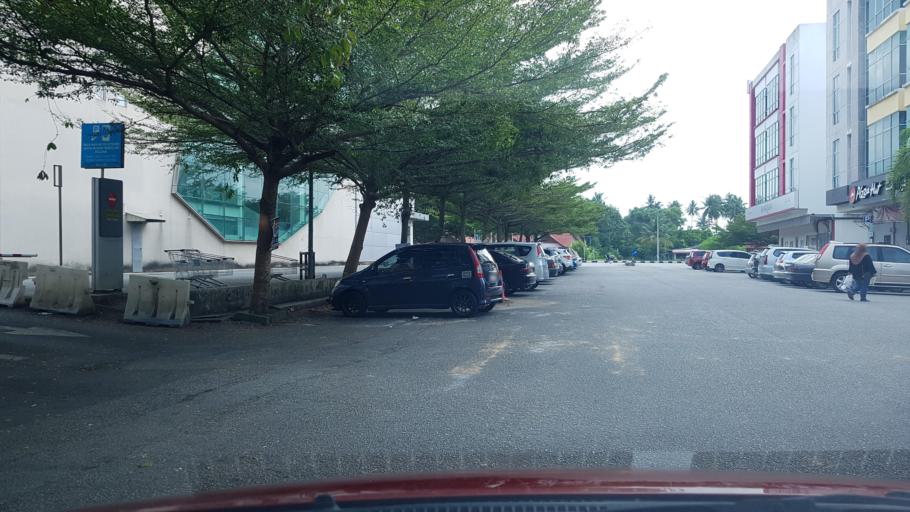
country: MY
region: Terengganu
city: Kuala Terengganu
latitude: 5.3560
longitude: 103.0960
